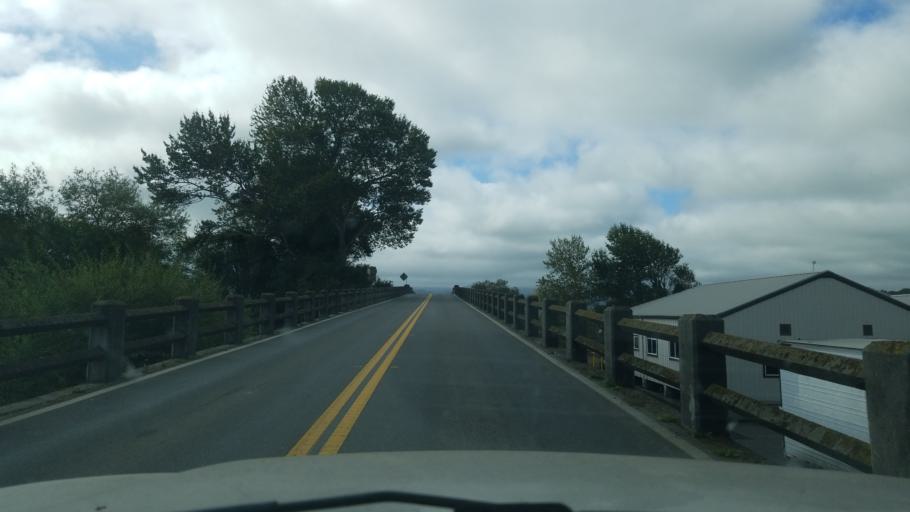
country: US
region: California
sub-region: Humboldt County
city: Fortuna
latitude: 40.6155
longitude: -124.2022
